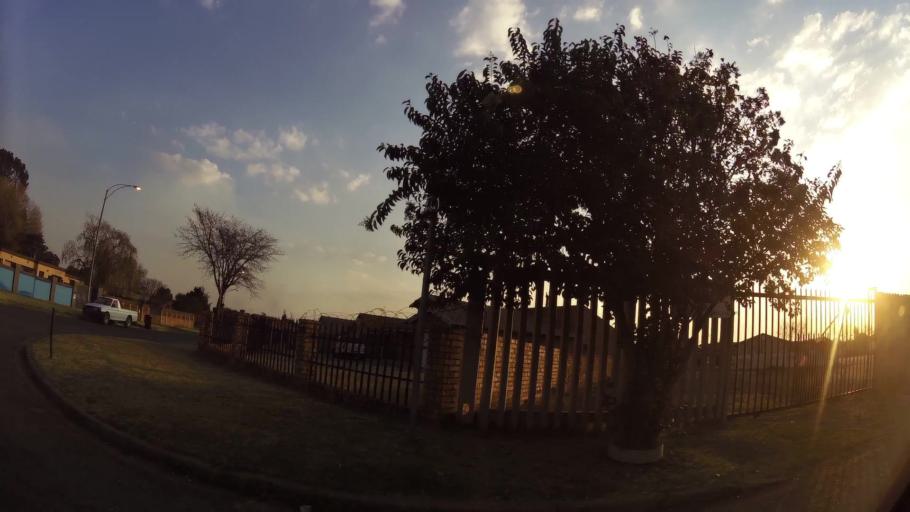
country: ZA
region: Gauteng
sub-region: Ekurhuleni Metropolitan Municipality
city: Springs
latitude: -26.2652
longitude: 28.4105
